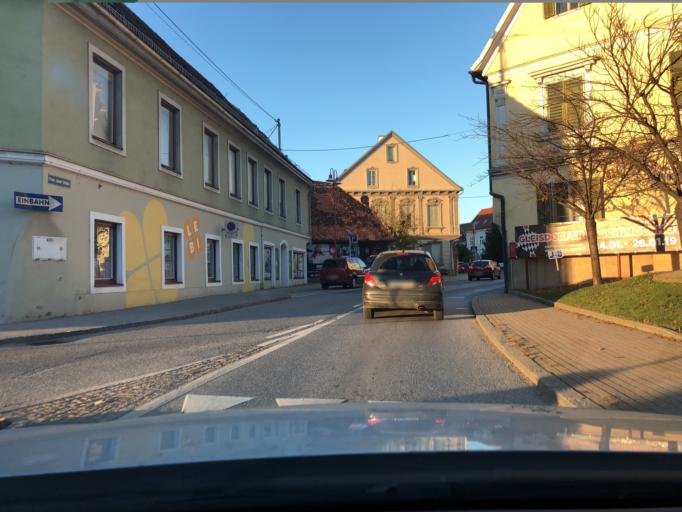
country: AT
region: Styria
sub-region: Politischer Bezirk Weiz
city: Gleisdorf
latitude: 47.1041
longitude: 15.7112
